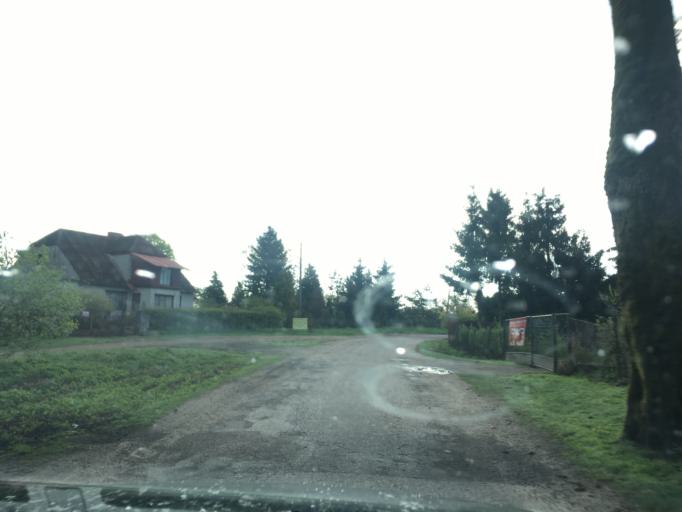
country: PL
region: Warmian-Masurian Voivodeship
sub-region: Powiat ostrodzki
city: Dabrowno
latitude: 53.4363
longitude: 19.9897
